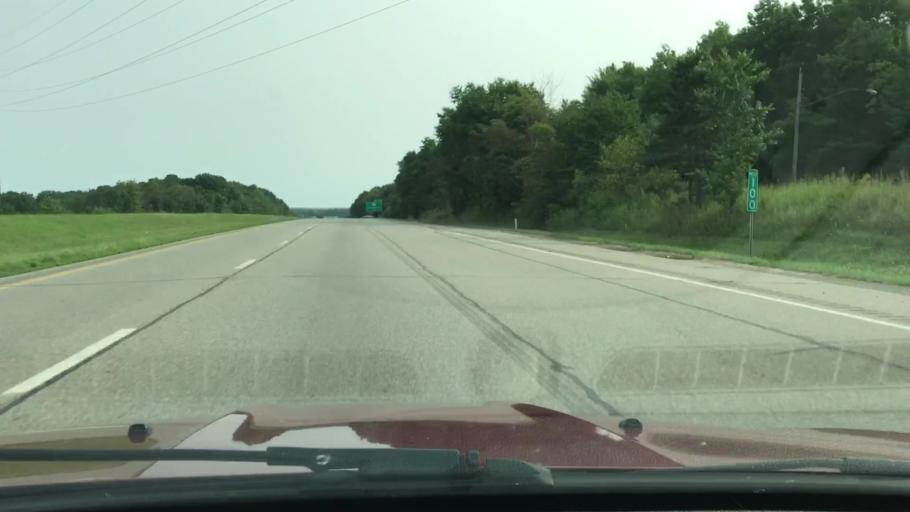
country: US
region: Ohio
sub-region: Stark County
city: Richville
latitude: 40.7334
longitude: -81.4154
